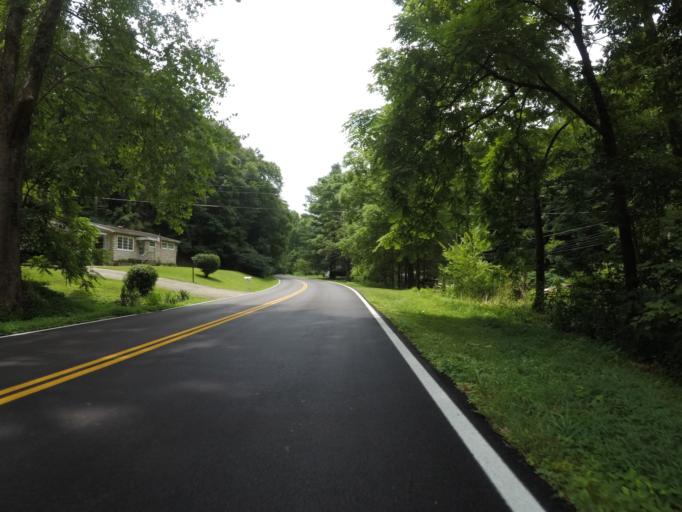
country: US
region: Kentucky
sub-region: Boyd County
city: Catlettsburg
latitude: 38.4257
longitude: -82.6275
